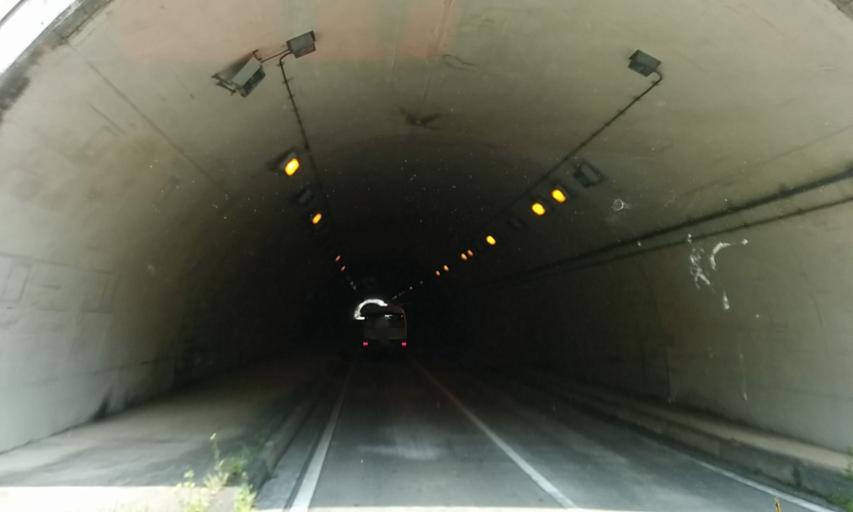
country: JP
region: Ehime
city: Niihama
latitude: 33.8861
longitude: 133.3051
